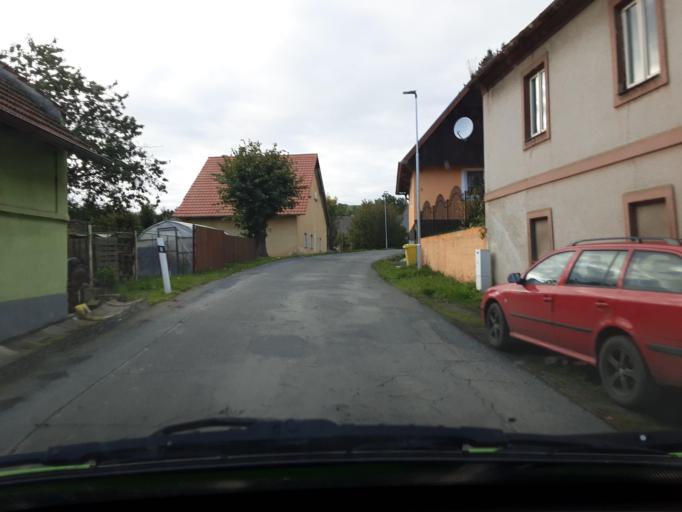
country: CZ
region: Plzensky
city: Janovice nad Uhlavou
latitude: 49.4249
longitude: 13.1769
